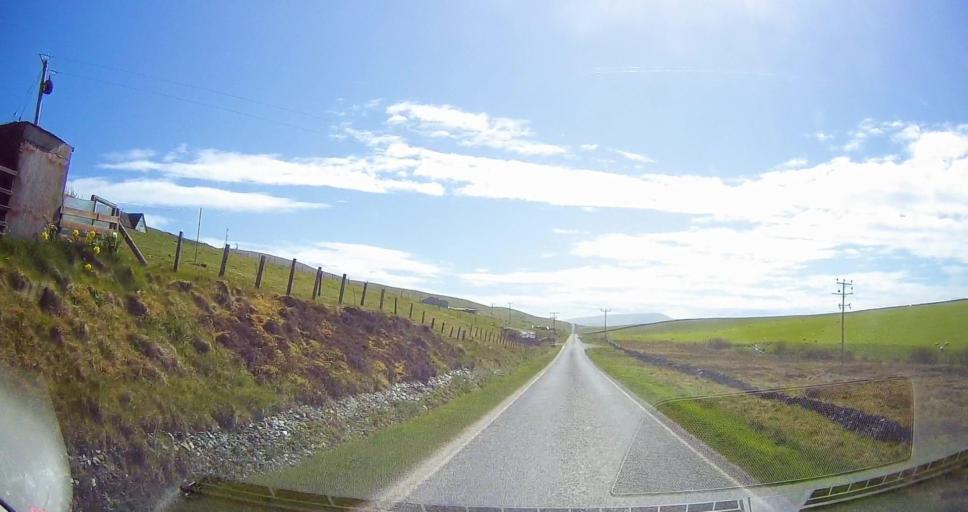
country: GB
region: Scotland
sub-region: Shetland Islands
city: Sandwick
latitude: 59.9717
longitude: -1.3162
